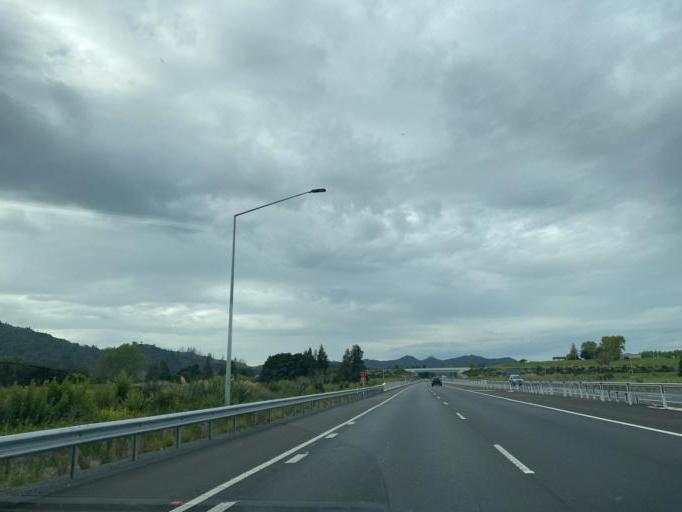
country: NZ
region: Waikato
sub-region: Waikato District
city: Ngaruawahia
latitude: -37.6160
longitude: 175.2048
